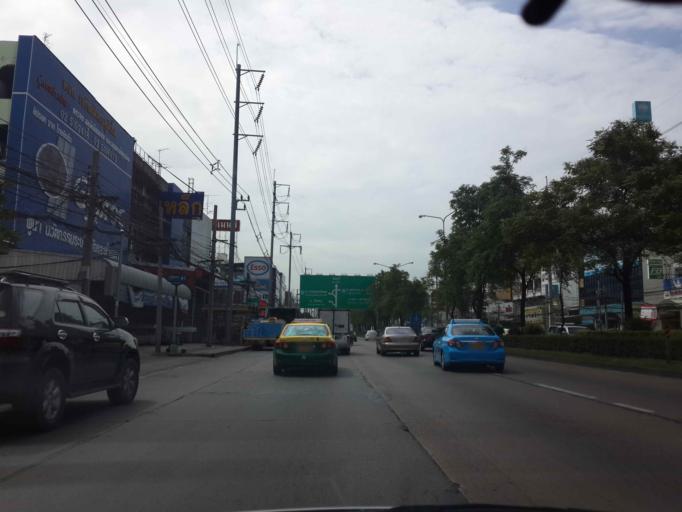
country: TH
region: Bangkok
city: Bang Khen
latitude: 13.8553
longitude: 100.6318
